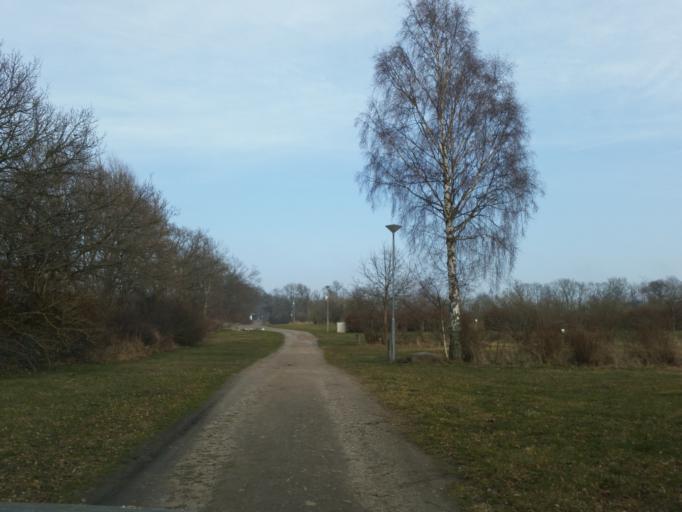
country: SE
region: Kalmar
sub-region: Borgholms Kommun
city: Borgholm
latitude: 56.9056
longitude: 16.7269
